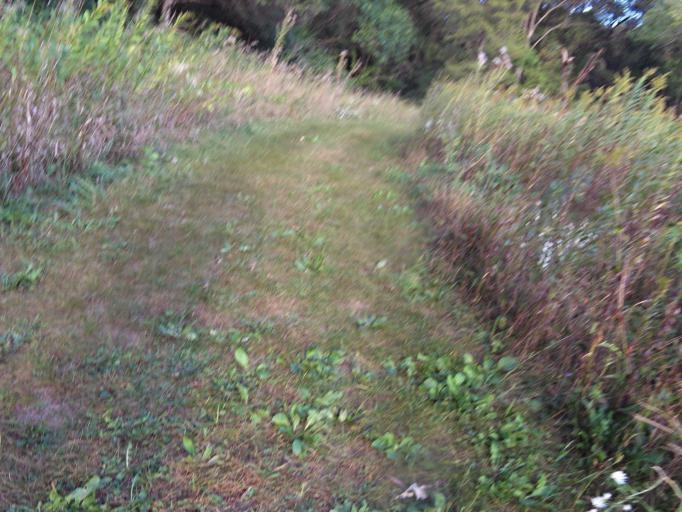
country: US
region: Minnesota
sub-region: Washington County
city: Lakeland
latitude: 44.9397
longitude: -92.7923
